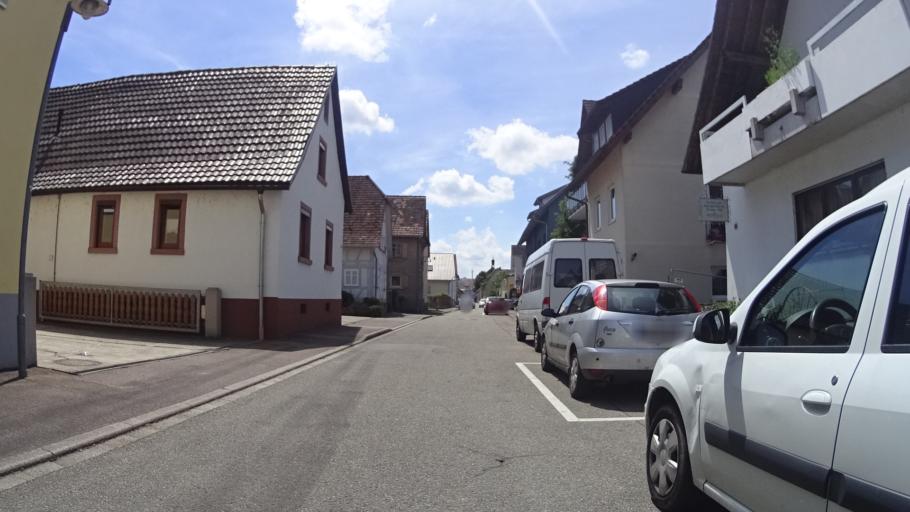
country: DE
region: Baden-Wuerttemberg
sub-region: Freiburg Region
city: Kappel-Grafenhausen
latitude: 48.2942
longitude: 7.7431
